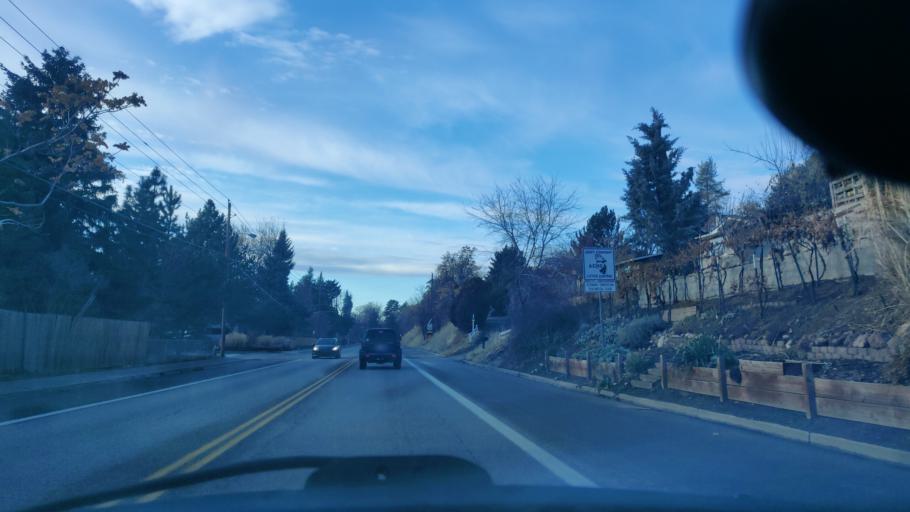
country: US
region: Idaho
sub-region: Ada County
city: Boise
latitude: 43.6412
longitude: -116.2102
